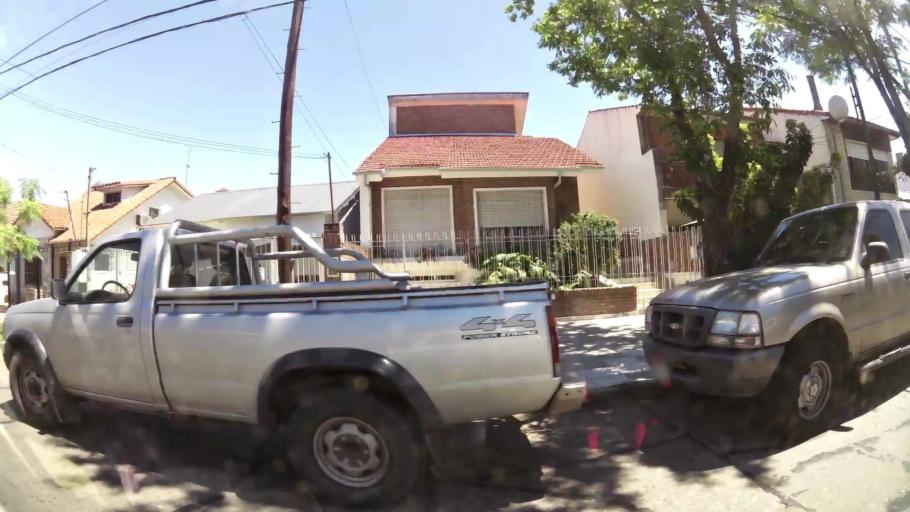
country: AR
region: Buenos Aires
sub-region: Partido de San Isidro
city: San Isidro
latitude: -34.5109
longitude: -58.5698
